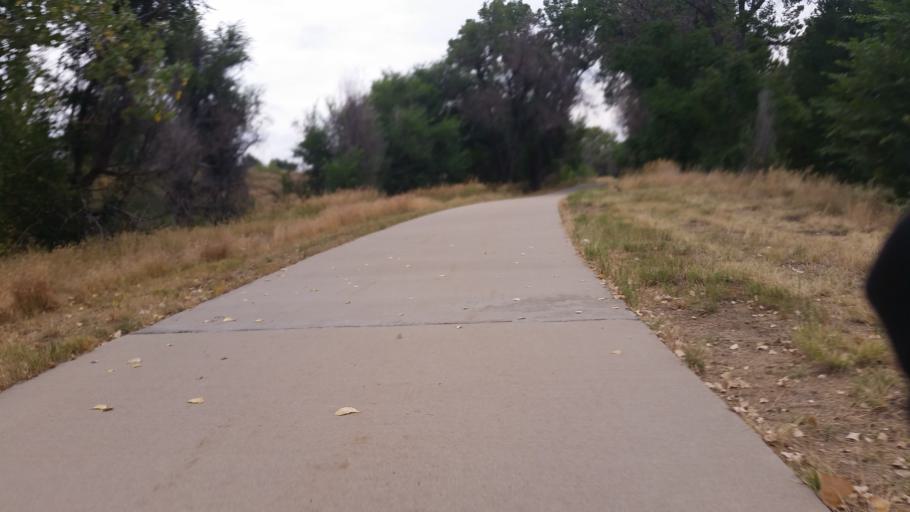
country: US
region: Colorado
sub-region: Adams County
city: Welby
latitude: 39.8232
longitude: -104.9772
